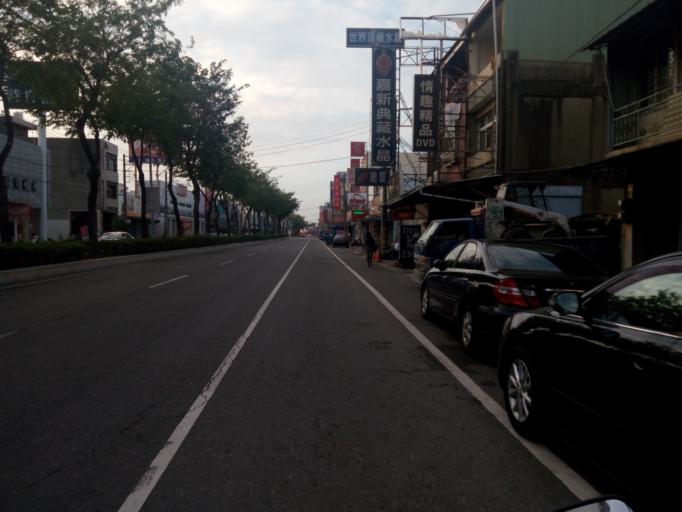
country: TW
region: Taiwan
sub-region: Chiayi
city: Jiayi Shi
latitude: 23.4825
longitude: 120.4262
